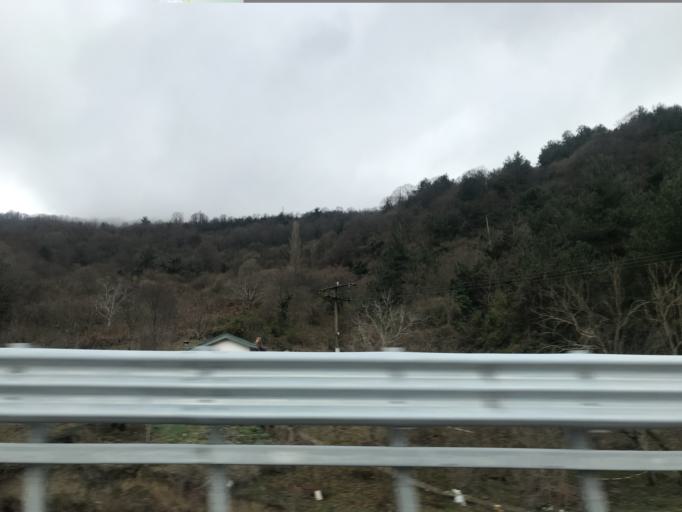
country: TR
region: Bartin
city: Amasra
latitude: 41.7333
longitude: 32.3730
